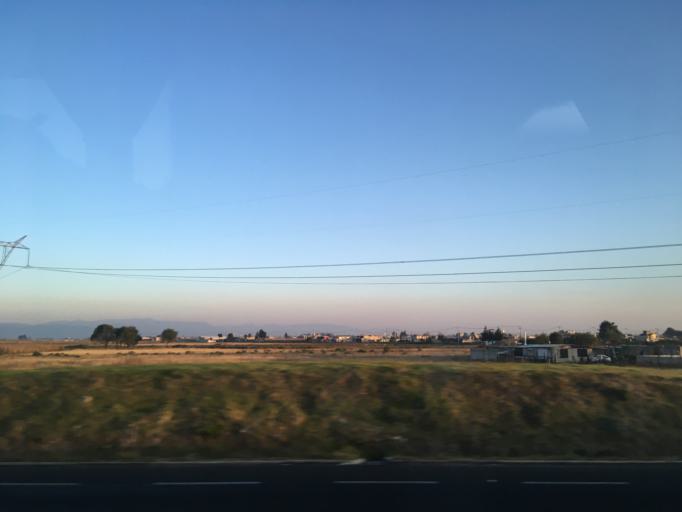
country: MX
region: Mexico
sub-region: Toluca
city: Galaxias Toluca
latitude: 19.3971
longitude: -99.6352
